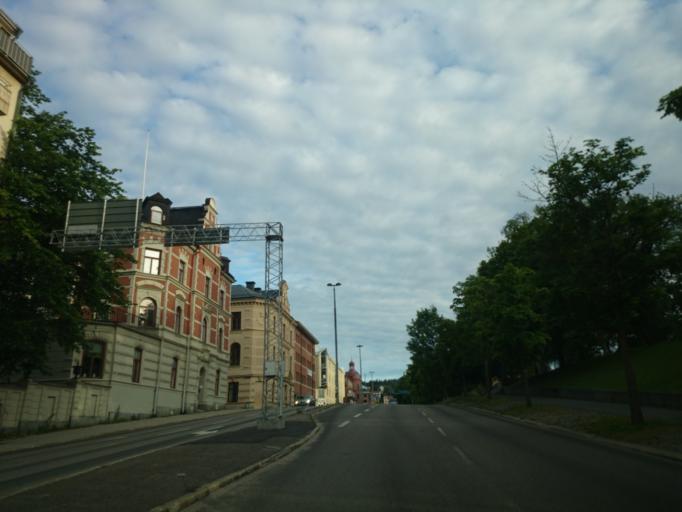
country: SE
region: Vaesternorrland
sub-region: Sundsvalls Kommun
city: Sundsvall
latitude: 62.3916
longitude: 17.3014
